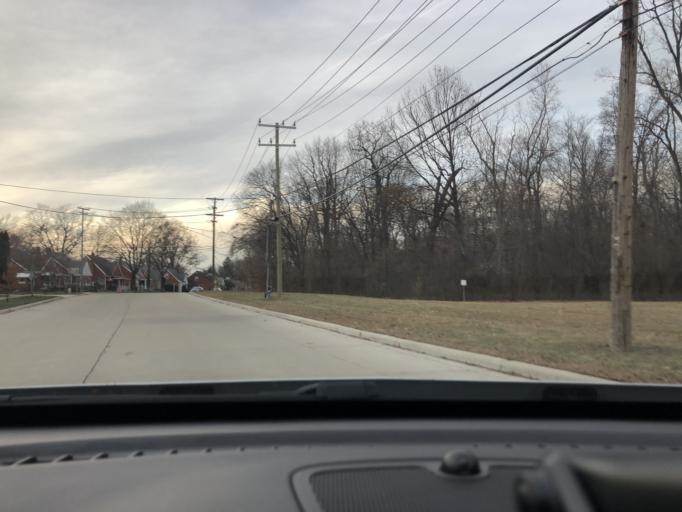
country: US
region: Michigan
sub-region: Wayne County
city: Allen Park
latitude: 42.2901
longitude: -83.2227
